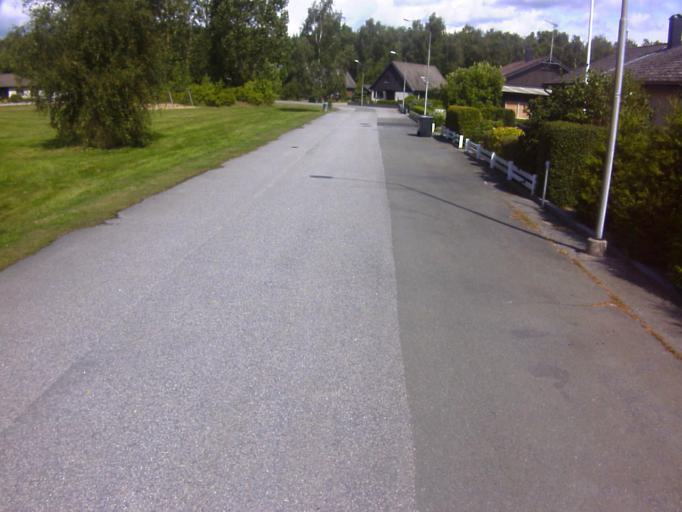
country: SE
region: Blekinge
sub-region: Solvesborgs Kommun
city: Soelvesborg
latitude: 56.0904
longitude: 14.6546
